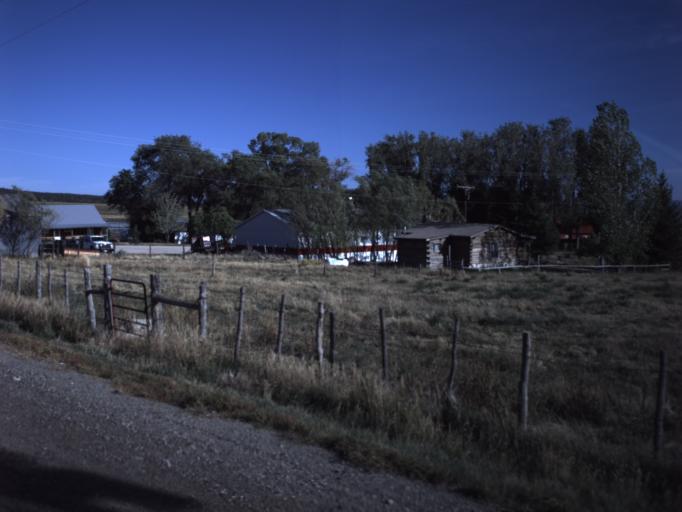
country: US
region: Utah
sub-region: Grand County
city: Moab
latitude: 38.3124
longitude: -109.2500
